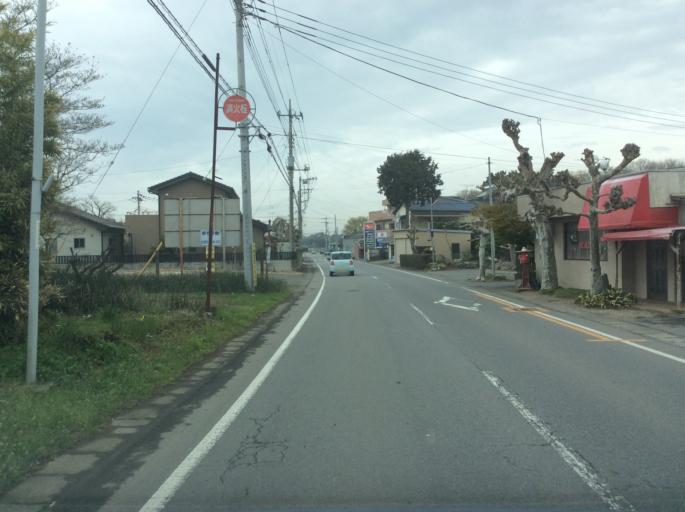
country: JP
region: Ibaraki
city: Iwai
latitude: 36.0037
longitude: 139.9082
